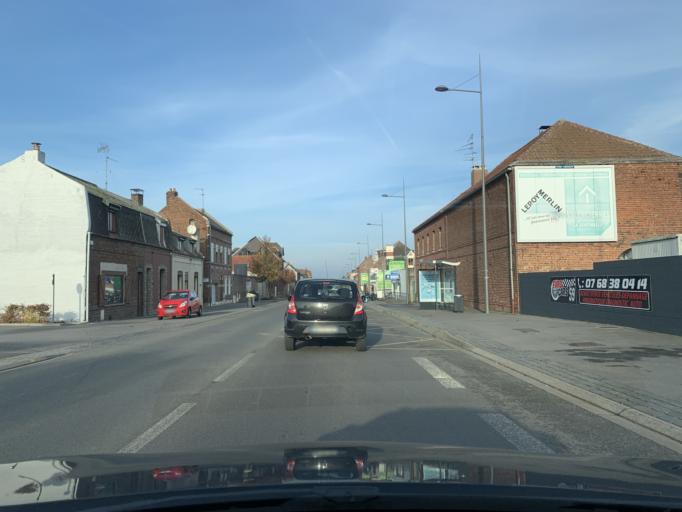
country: FR
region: Nord-Pas-de-Calais
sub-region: Departement du Nord
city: Cambrai
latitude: 50.1561
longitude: 3.2230
